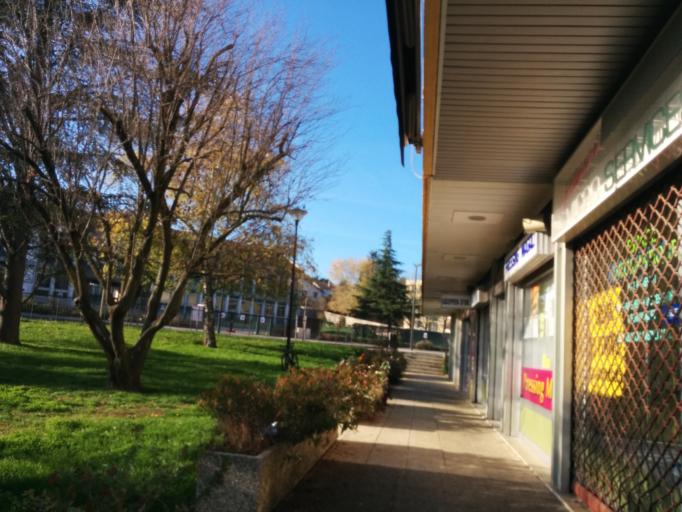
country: FR
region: Rhone-Alpes
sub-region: Departement de l'Ain
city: Meximieux
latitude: 45.9035
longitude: 5.1904
